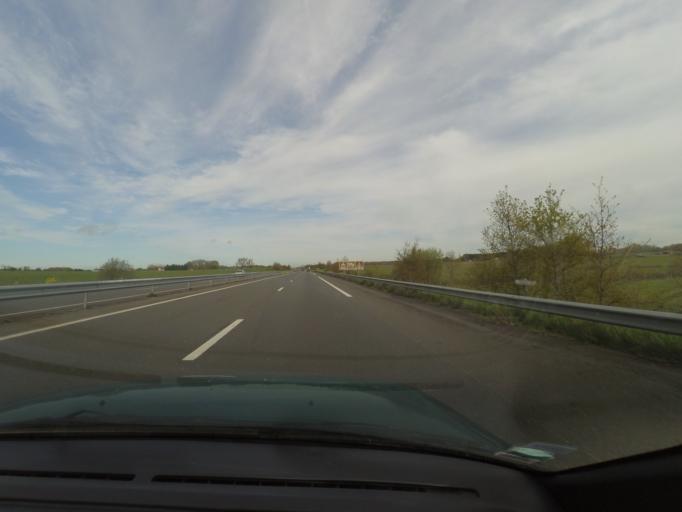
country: FR
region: Pays de la Loire
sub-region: Departement de la Loire-Atlantique
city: Le Bignon
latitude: 47.0946
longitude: -1.4651
